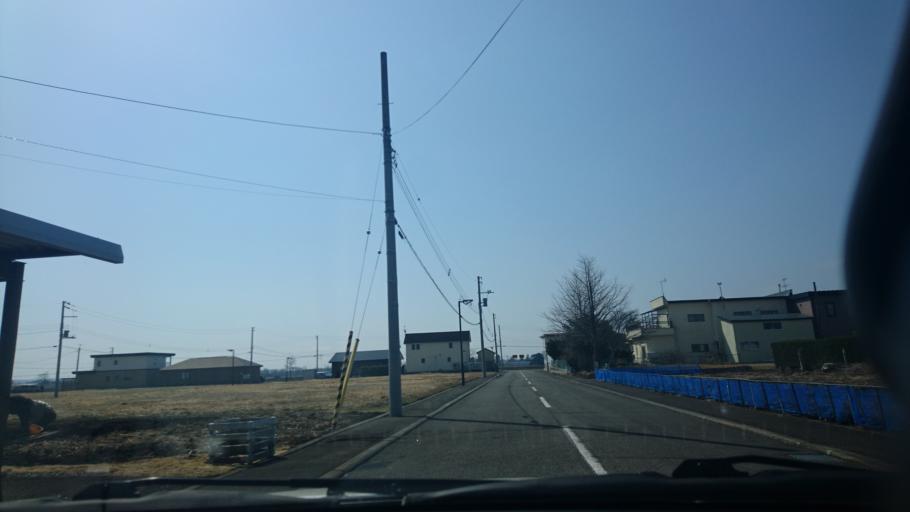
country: JP
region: Hokkaido
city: Otofuke
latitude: 43.0949
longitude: 143.2300
